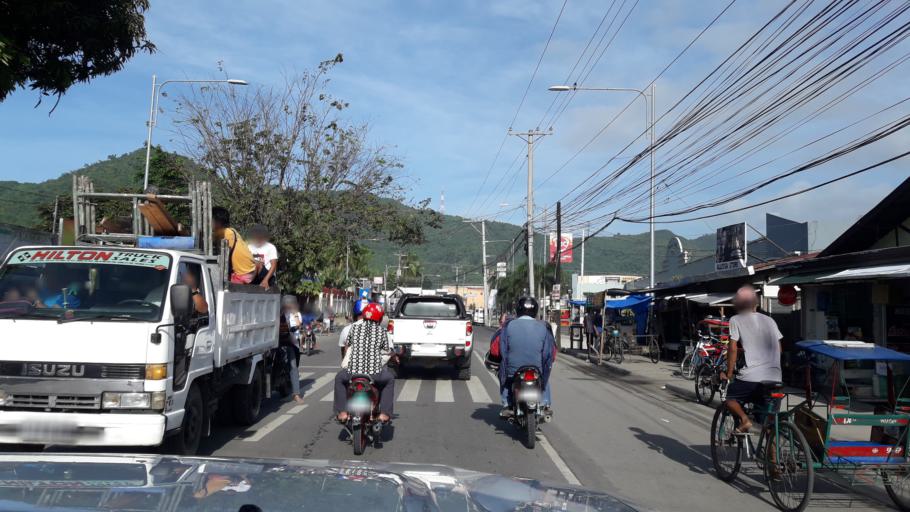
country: PH
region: Eastern Visayas
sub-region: Province of Leyte
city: Panalanoy
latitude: 11.2162
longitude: 124.9963
